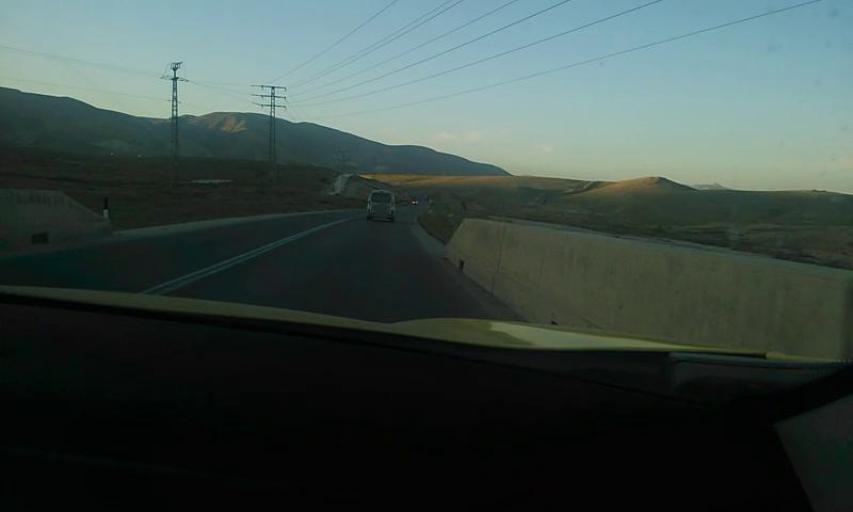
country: PS
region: West Bank
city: An Nuway`imah
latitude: 31.9178
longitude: 35.4198
